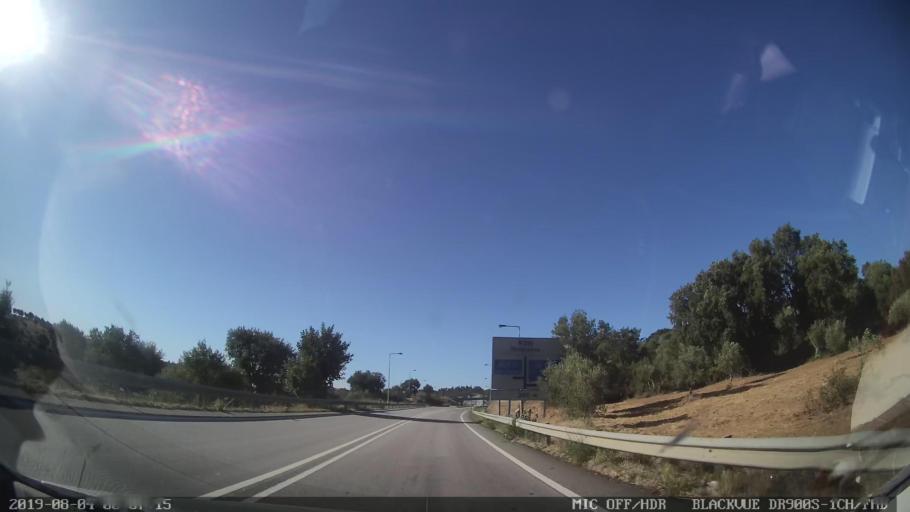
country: PT
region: Santarem
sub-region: Abrantes
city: Alferrarede
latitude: 39.4893
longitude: -8.0989
